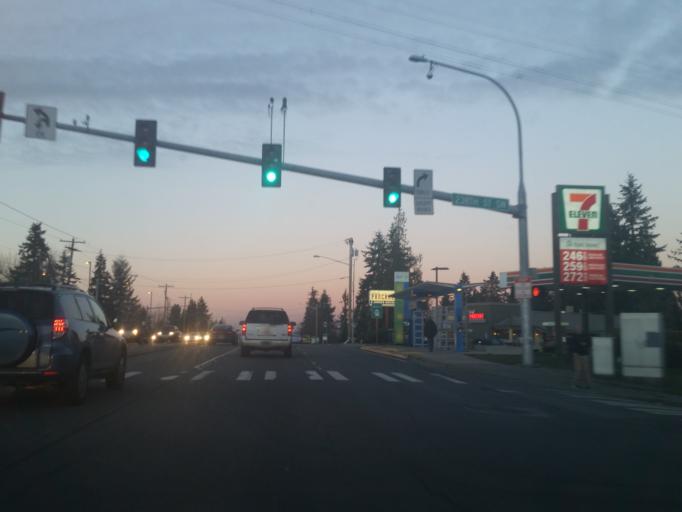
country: US
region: Washington
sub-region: Snohomish County
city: Esperance
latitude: 47.7833
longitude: -122.3434
